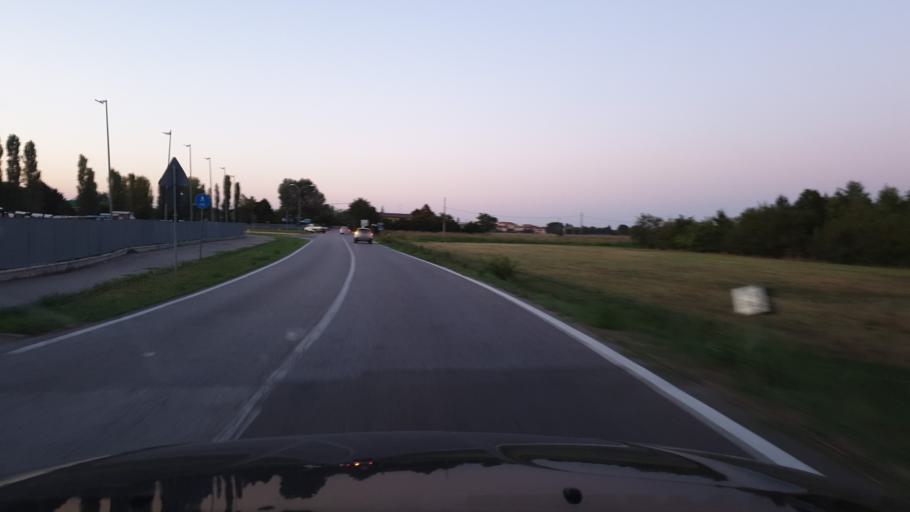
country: IT
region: Emilia-Romagna
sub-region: Provincia di Bologna
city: Altedo
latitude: 44.6811
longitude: 11.4967
